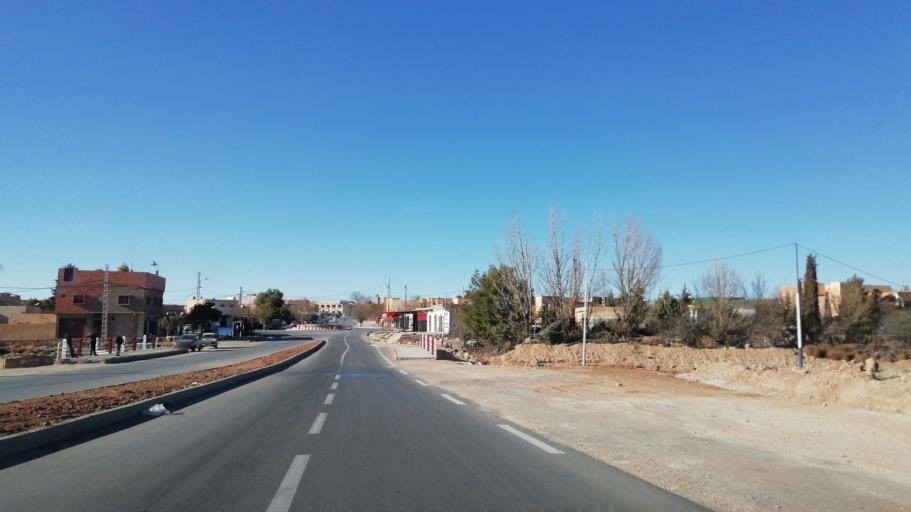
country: DZ
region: Tlemcen
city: Sebdou
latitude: 34.2233
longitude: -1.2523
